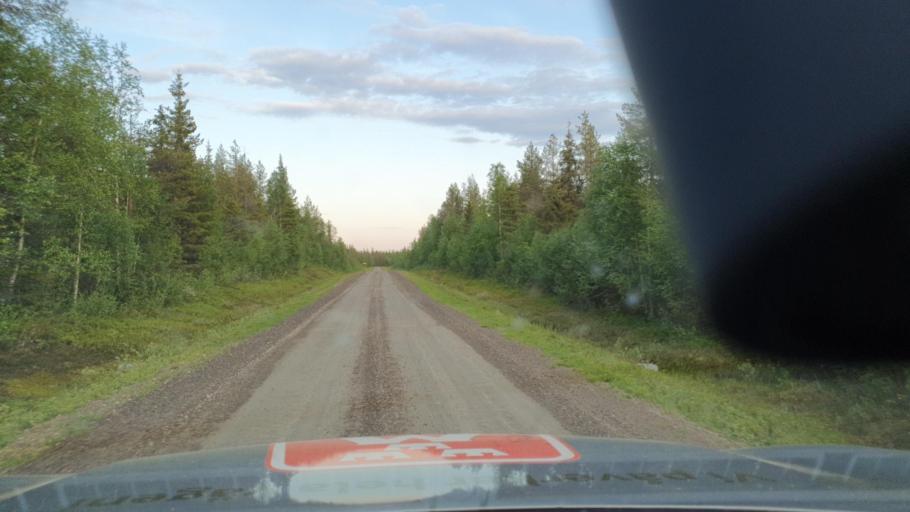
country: SE
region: Norrbotten
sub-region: Bodens Kommun
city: Boden
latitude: 66.5092
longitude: 21.5353
